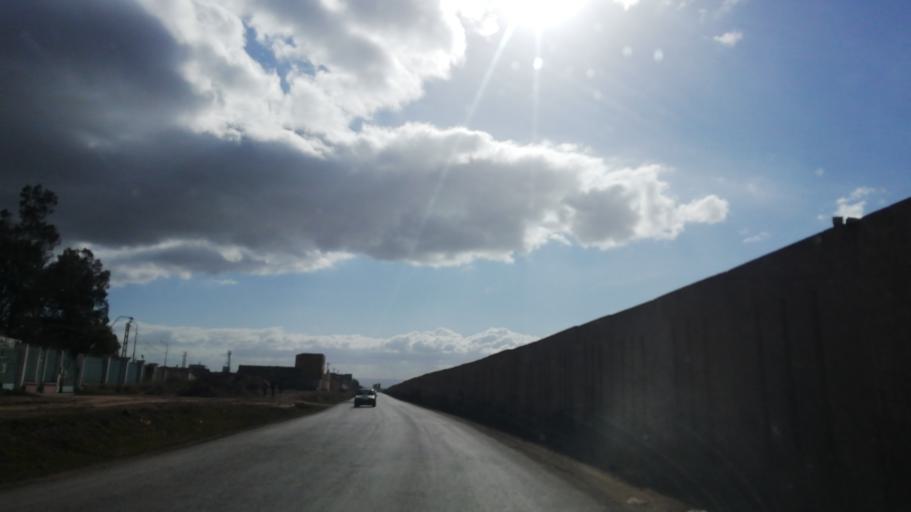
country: DZ
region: Oran
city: Es Senia
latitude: 35.6481
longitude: -0.6059
